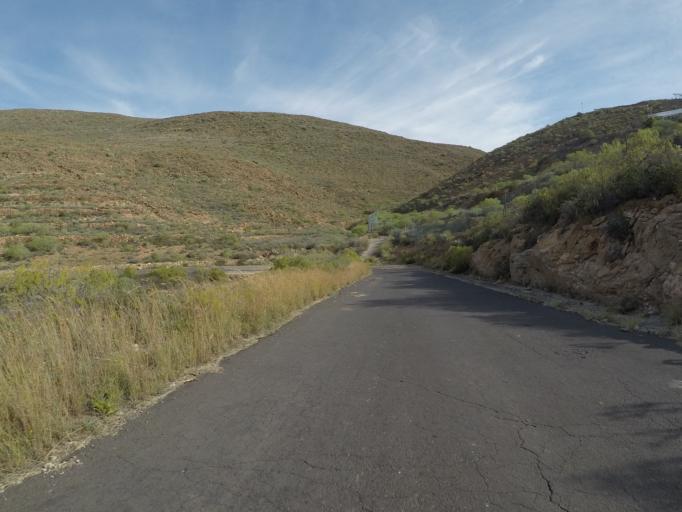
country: ES
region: Canary Islands
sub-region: Provincia de Santa Cruz de Tenerife
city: Lomo de Arico
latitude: 28.1553
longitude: -16.4881
